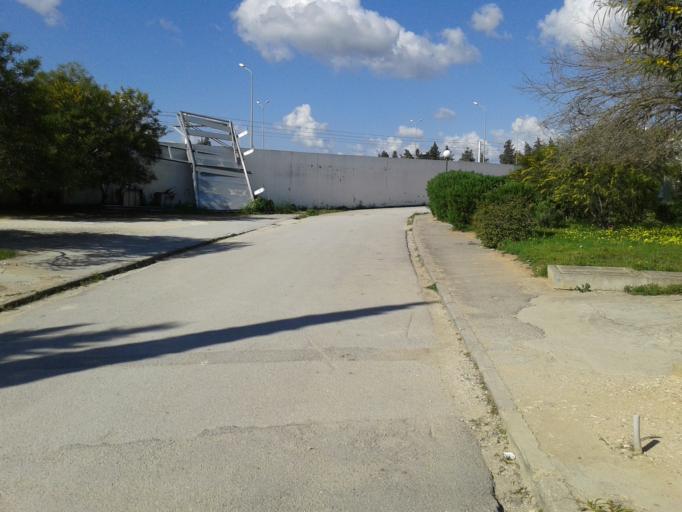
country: TN
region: Manouba
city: Manouba
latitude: 36.8114
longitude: 10.0660
